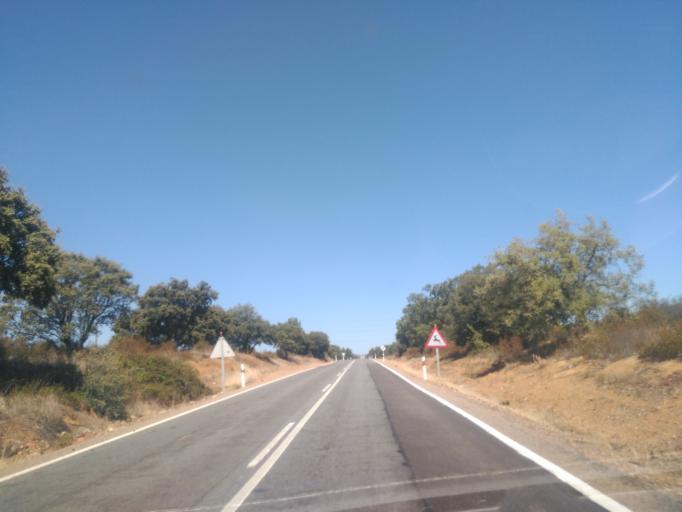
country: ES
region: Castille and Leon
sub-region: Provincia de Zamora
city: Pozuelo de Tabara
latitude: 41.8047
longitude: -5.9251
